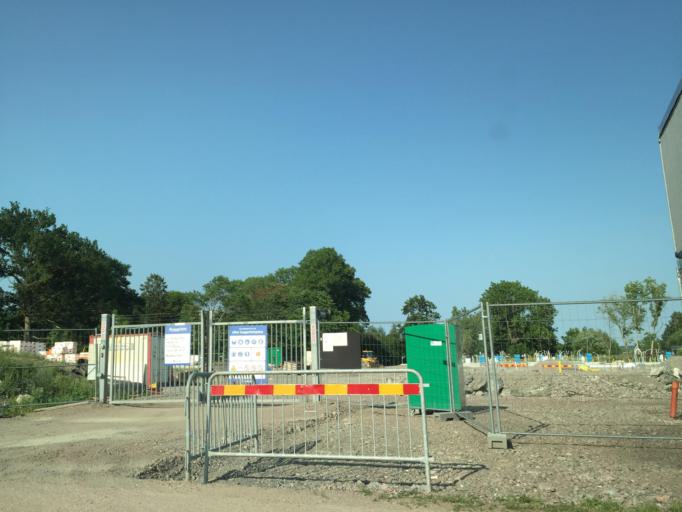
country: SE
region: Vaestra Goetaland
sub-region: Vanersborgs Kommun
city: Vanersborg
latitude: 58.3603
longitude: 12.3192
